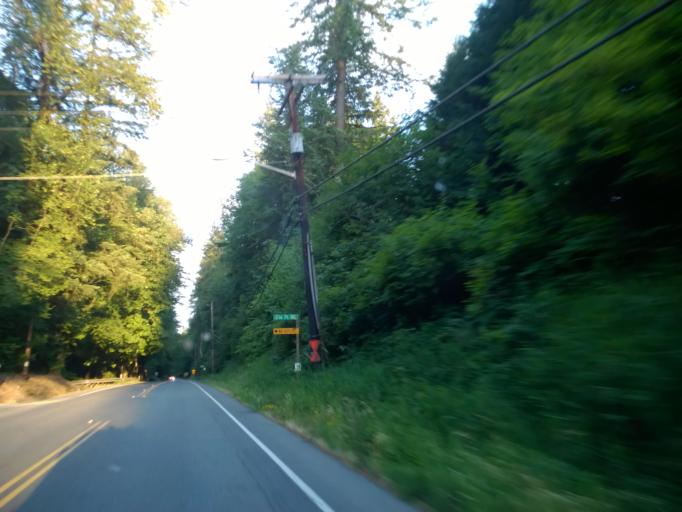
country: US
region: Washington
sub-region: King County
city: Duvall
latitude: 47.7555
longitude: -122.0230
